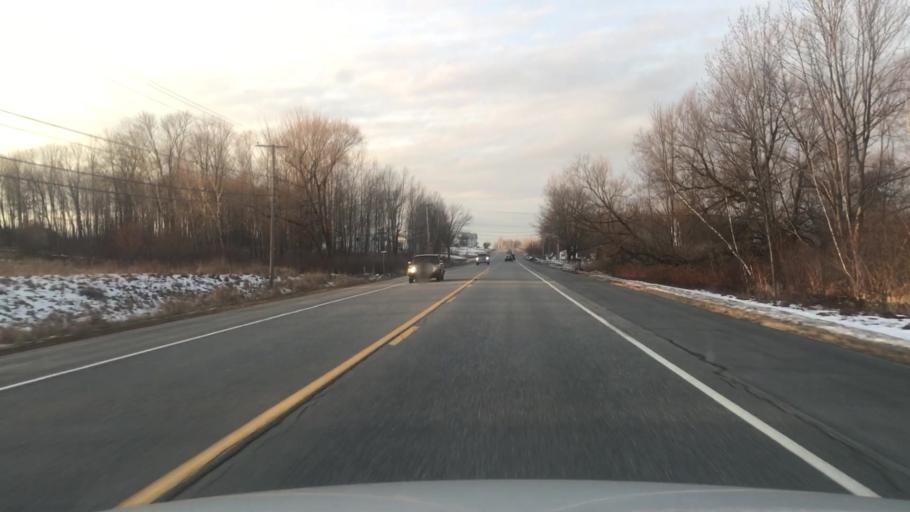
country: US
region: Maine
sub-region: Somerset County
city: Fairfield
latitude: 44.6355
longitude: -69.5979
